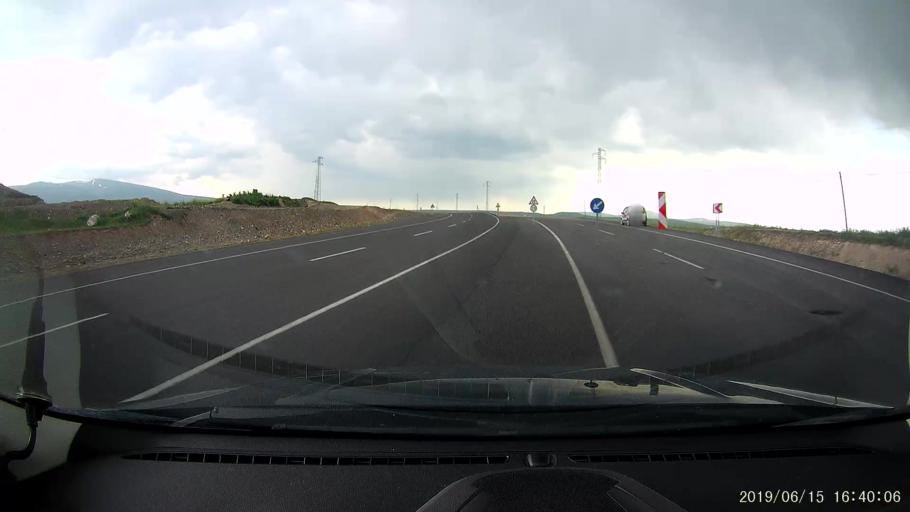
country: TR
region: Ardahan
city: Haskoy
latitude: 40.9737
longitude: 42.8939
